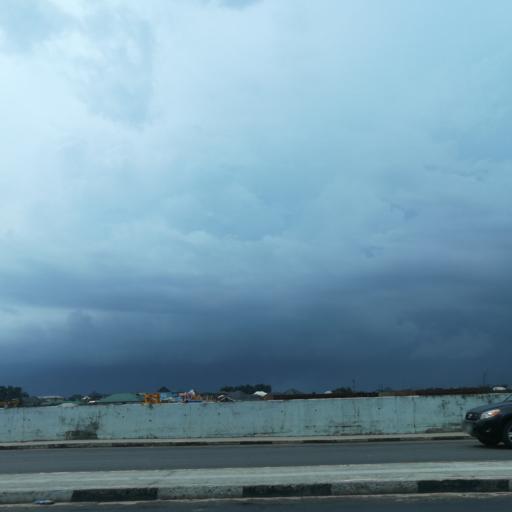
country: NG
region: Rivers
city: Port Harcourt
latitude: 4.8038
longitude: 7.0579
